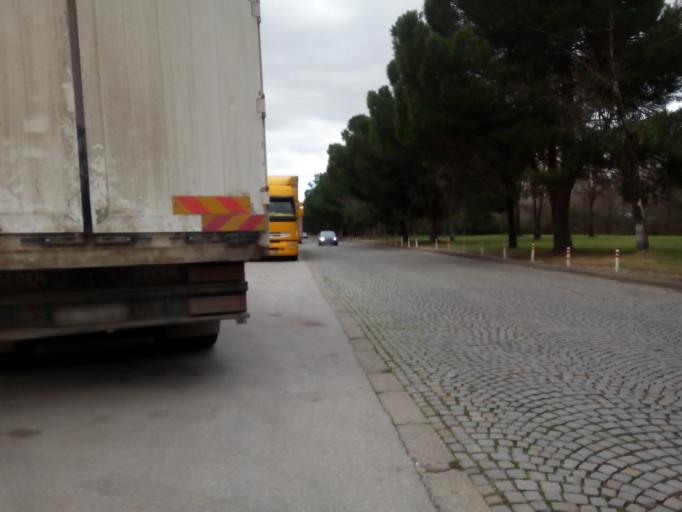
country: TR
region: Bursa
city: Niluefer
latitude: 40.2457
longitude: 28.9628
